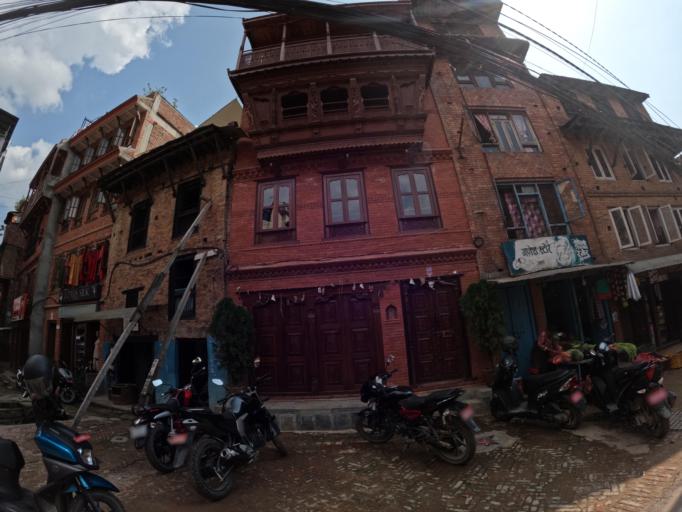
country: NP
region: Central Region
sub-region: Bagmati Zone
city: Bhaktapur
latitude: 27.6727
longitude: 85.4253
